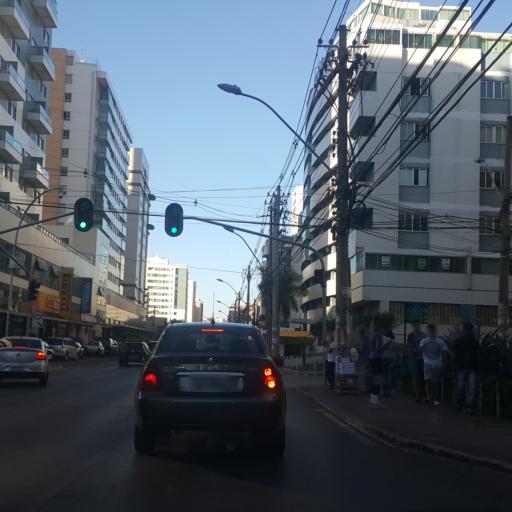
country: BR
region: Federal District
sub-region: Brasilia
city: Brasilia
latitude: -15.8412
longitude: -48.0234
